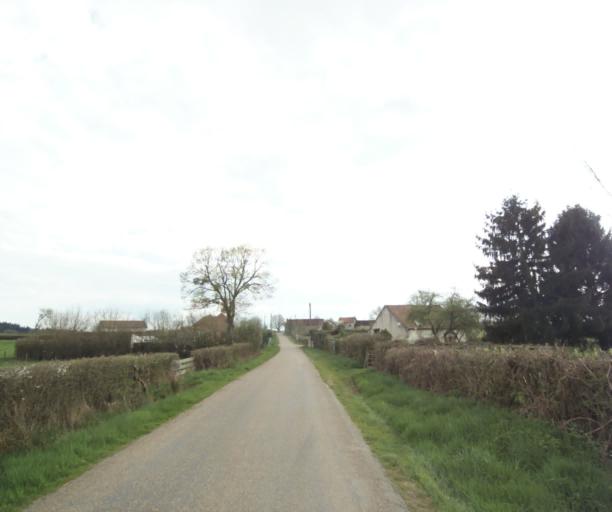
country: FR
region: Bourgogne
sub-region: Departement de Saone-et-Loire
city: Saint-Vallier
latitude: 46.5150
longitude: 4.3897
